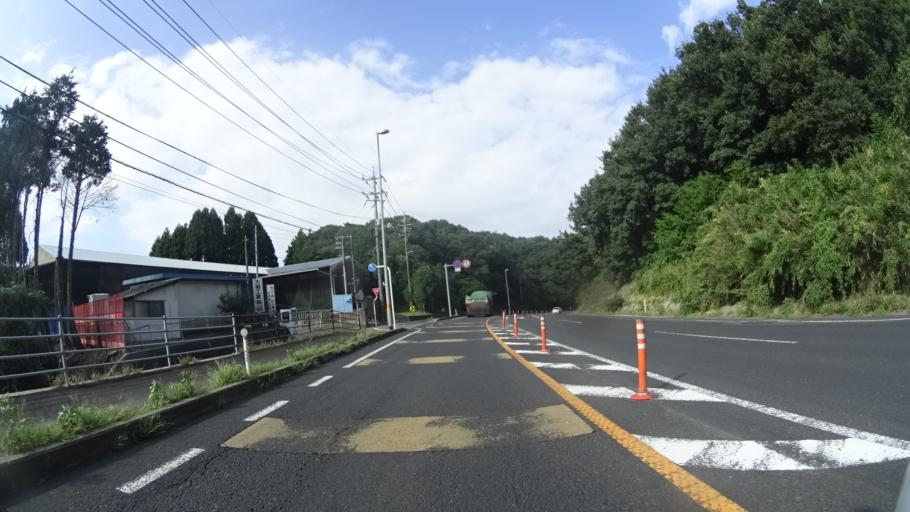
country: JP
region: Shimane
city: Odacho-oda
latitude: 35.2443
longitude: 132.5499
